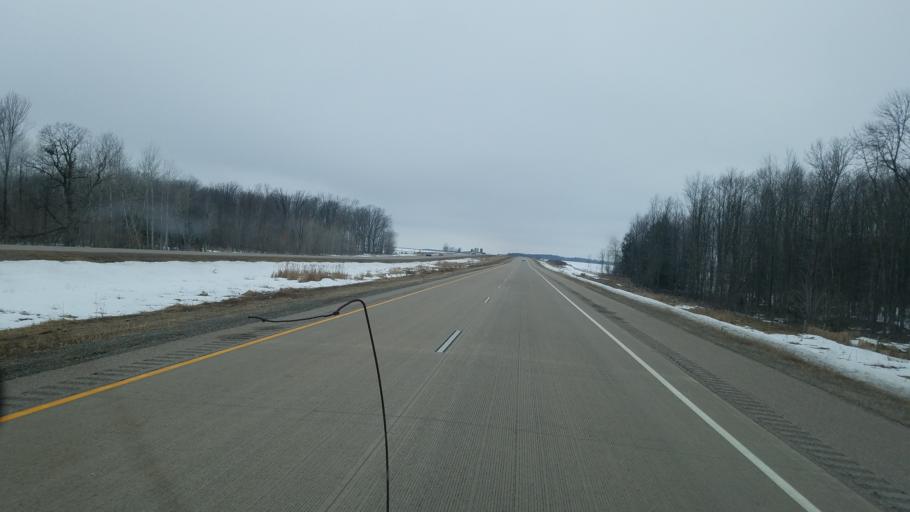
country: US
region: Wisconsin
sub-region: Wood County
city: Wisconsin Rapids
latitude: 44.6203
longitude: -89.8934
